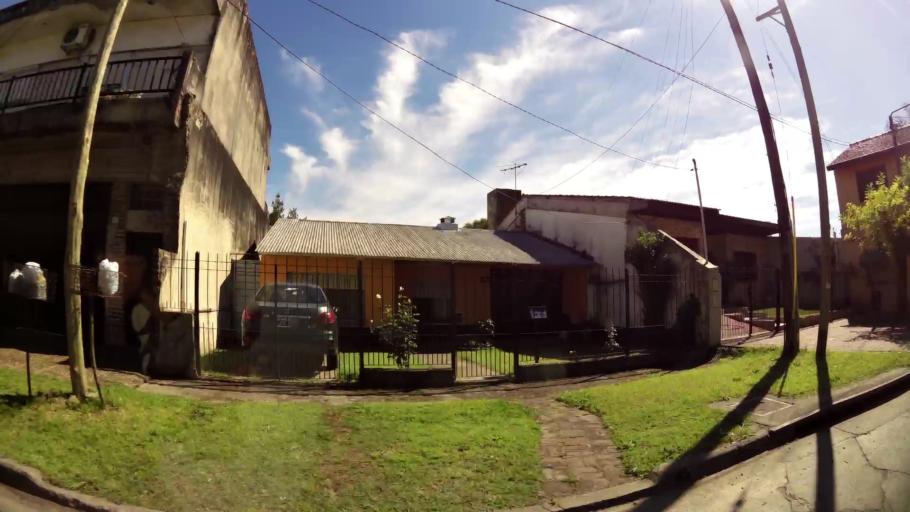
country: AR
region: Buenos Aires
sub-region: Partido de Quilmes
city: Quilmes
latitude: -34.6985
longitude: -58.2990
